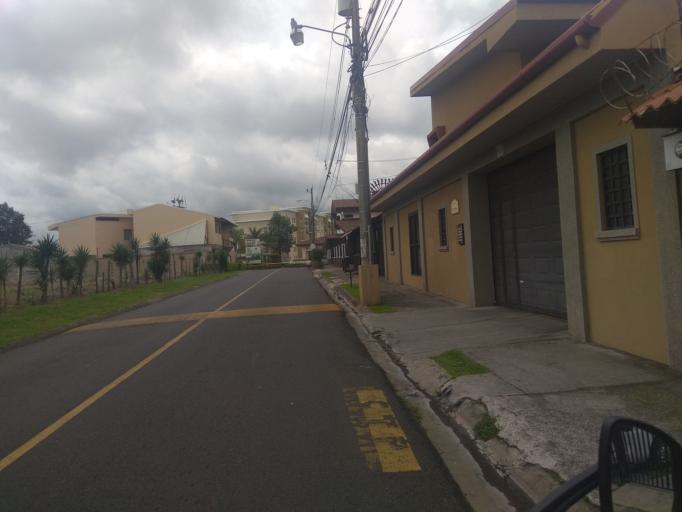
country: CR
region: Heredia
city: San Pablo
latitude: 10.0024
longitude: -84.1006
